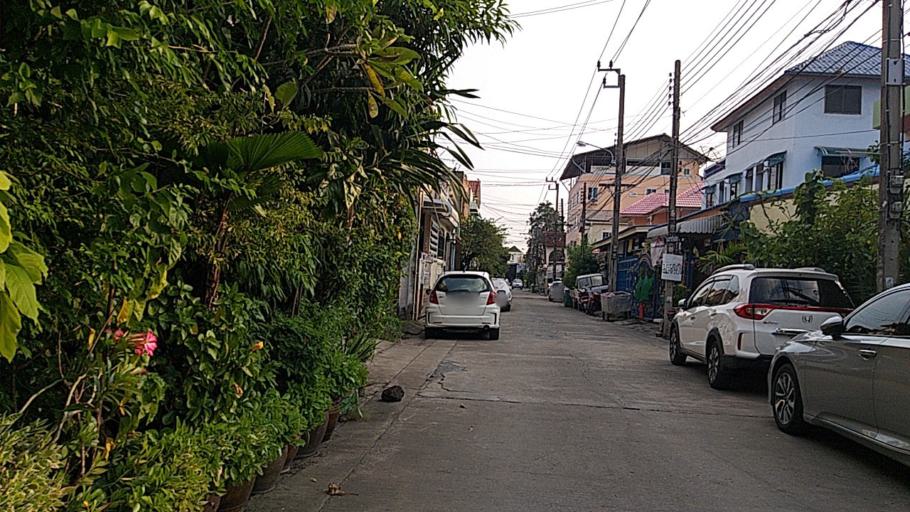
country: TH
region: Bangkok
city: Lat Phrao
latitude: 13.8257
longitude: 100.6217
